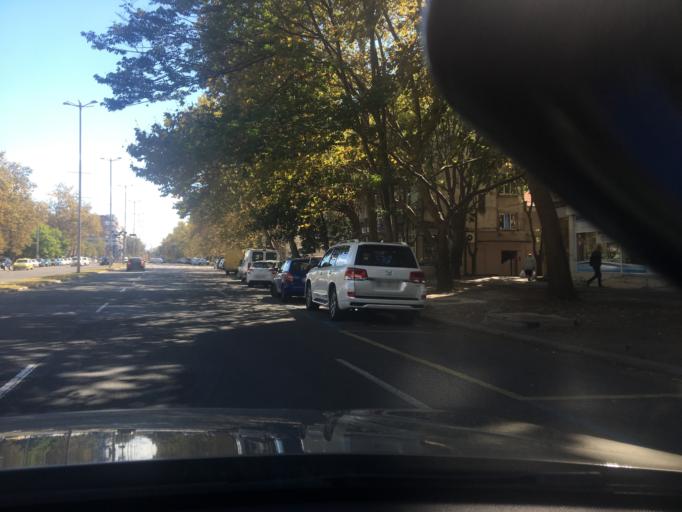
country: BG
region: Burgas
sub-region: Obshtina Burgas
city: Burgas
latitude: 42.5031
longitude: 27.4753
